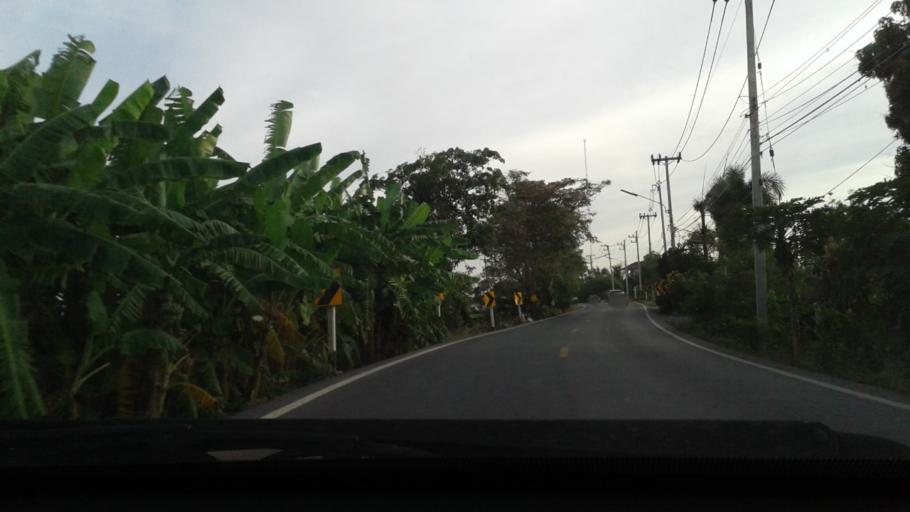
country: TH
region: Nonthaburi
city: Sai Noi
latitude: 13.9104
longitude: 100.2569
